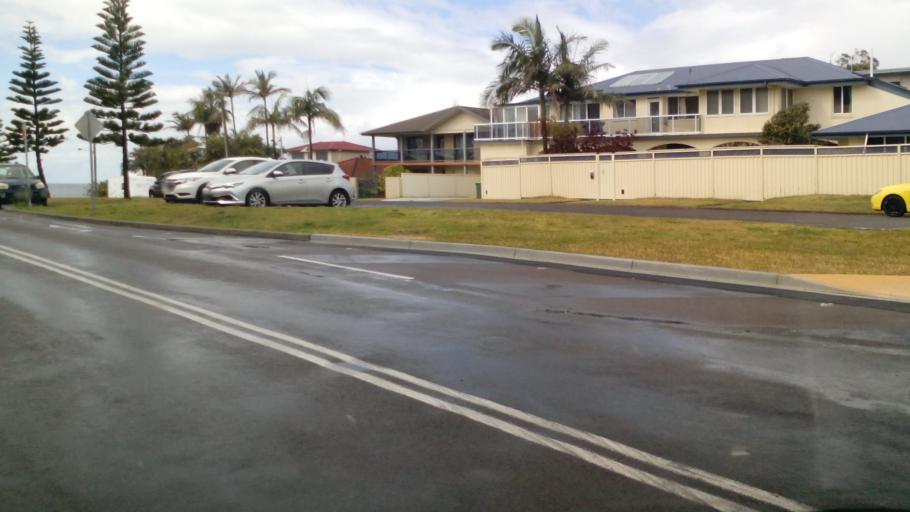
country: AU
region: New South Wales
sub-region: Lake Macquarie Shire
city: Belmont South
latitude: -33.1048
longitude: 151.6452
